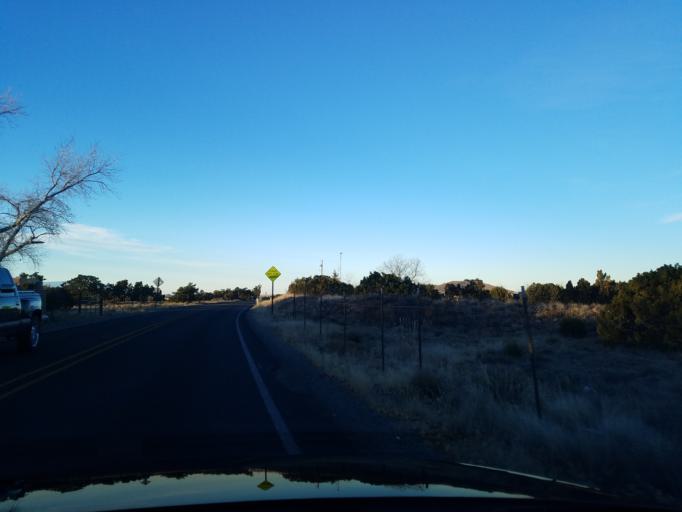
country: US
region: New Mexico
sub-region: Santa Fe County
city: Agua Fria
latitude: 35.6702
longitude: -106.0065
